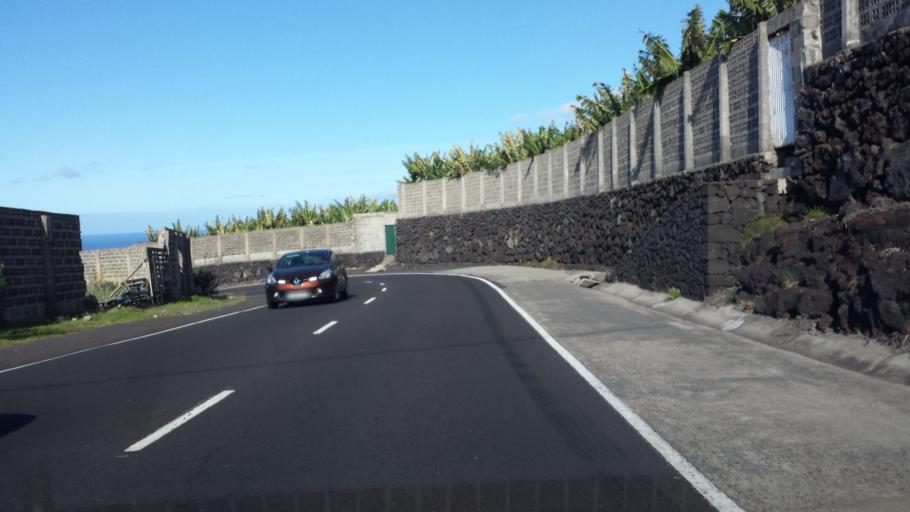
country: ES
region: Canary Islands
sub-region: Provincia de Santa Cruz de Tenerife
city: Tazacorte
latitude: 28.5982
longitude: -17.9113
